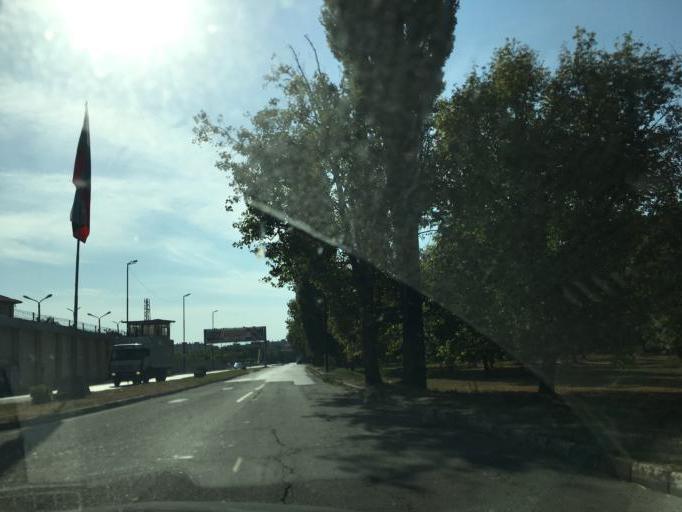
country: BG
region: Pazardzhik
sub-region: Obshtina Pazardzhik
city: Pazardzhik
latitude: 42.2098
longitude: 24.3250
